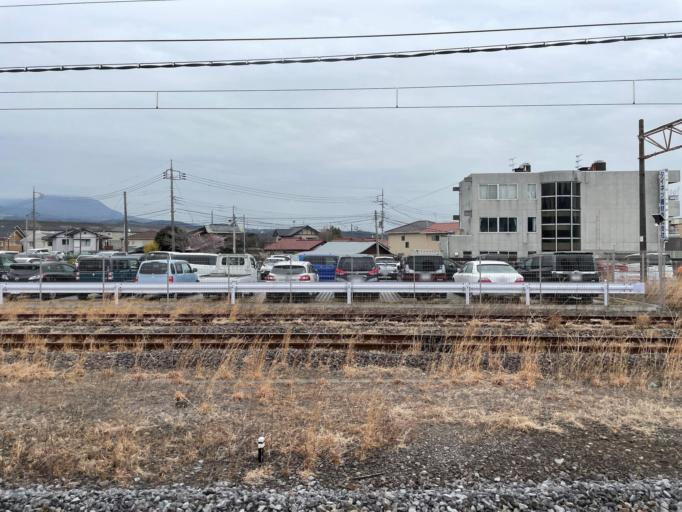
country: JP
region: Gunma
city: Shibukawa
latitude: 36.4897
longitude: 139.0083
